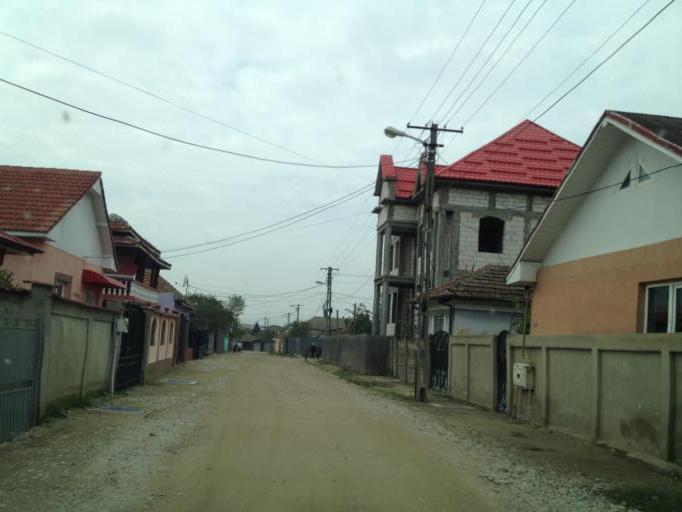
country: RO
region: Dolj
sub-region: Municipiul Craiova
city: Popoveni
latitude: 44.2884
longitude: 23.8025
